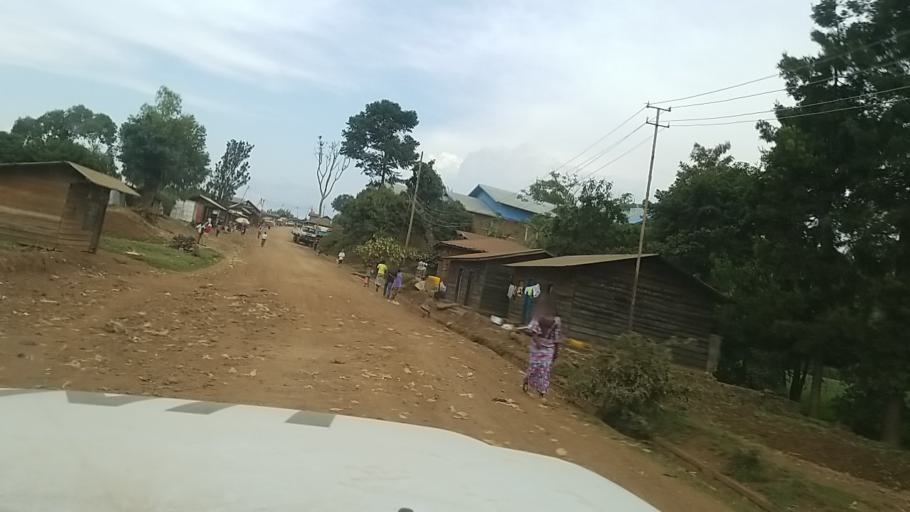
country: RW
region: Western Province
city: Cyangugu
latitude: -2.1753
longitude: 28.8552
